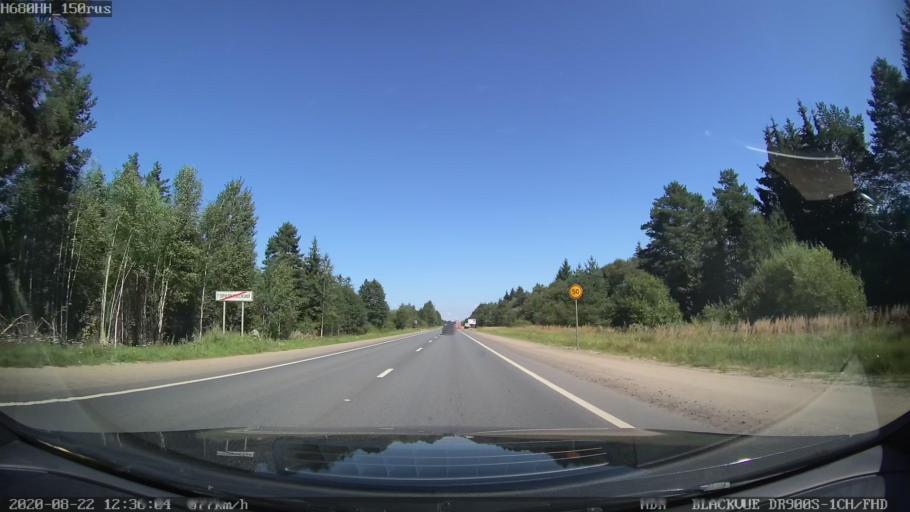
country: RU
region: Tverskaya
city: Rameshki
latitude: 57.2784
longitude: 36.0774
